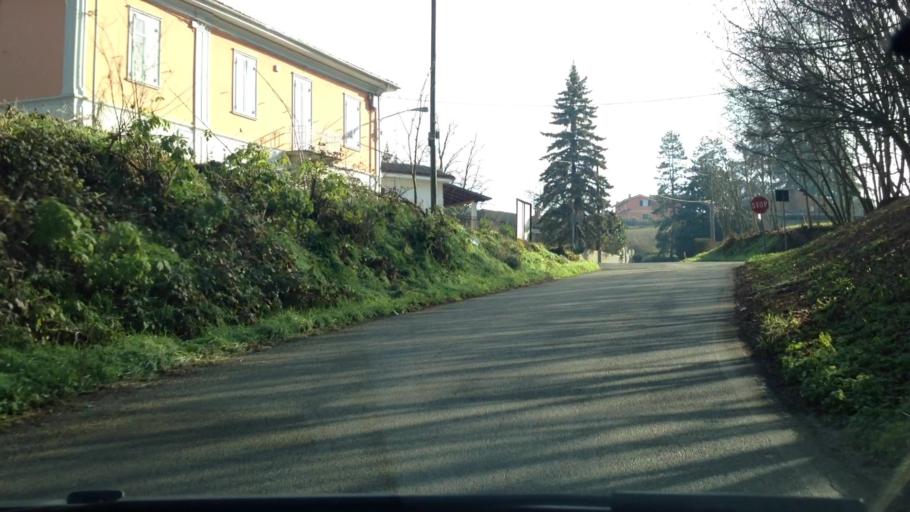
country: IT
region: Piedmont
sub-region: Provincia di Alessandria
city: Masio
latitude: 44.8541
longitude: 8.4156
